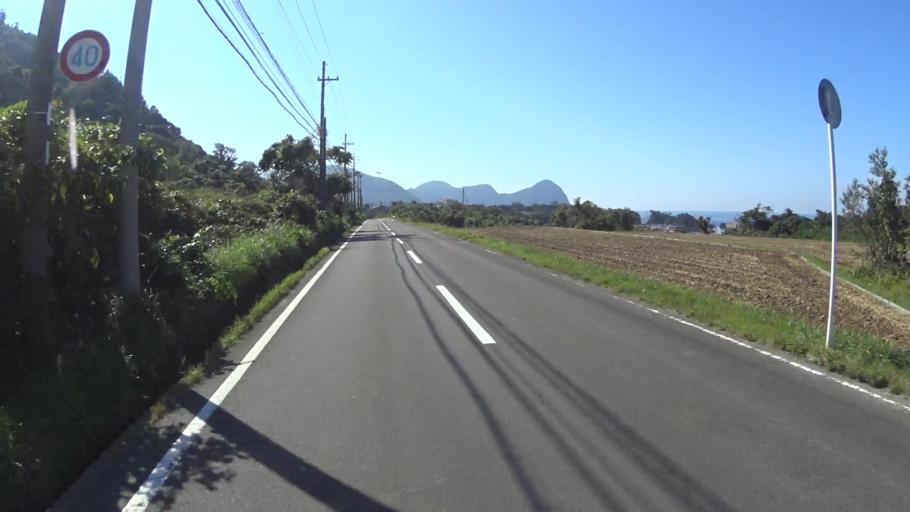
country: JP
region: Kyoto
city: Miyazu
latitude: 35.7621
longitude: 135.1852
